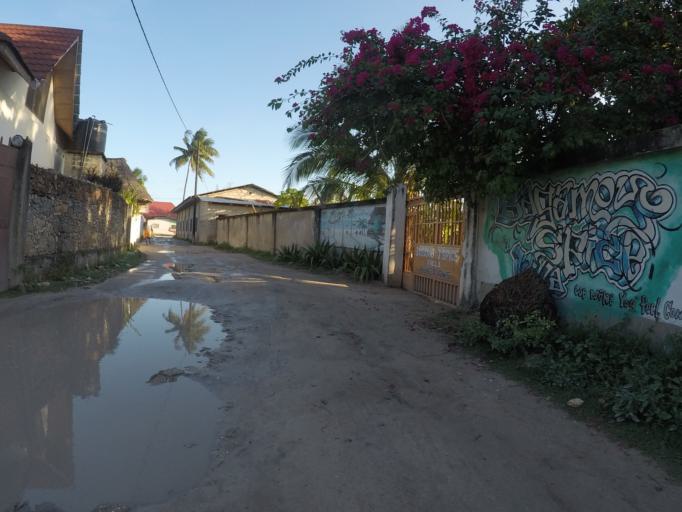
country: TZ
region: Zanzibar North
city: Nungwi
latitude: -5.7268
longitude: 39.2935
